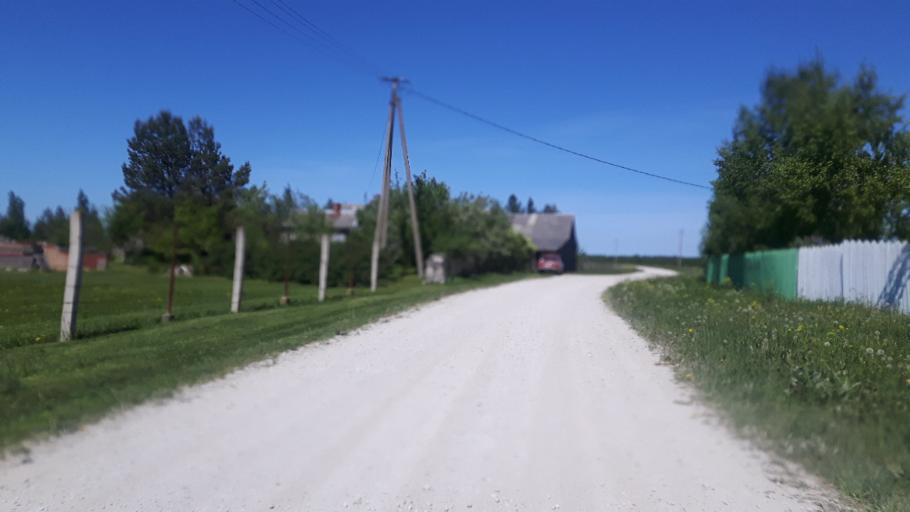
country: EE
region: Ida-Virumaa
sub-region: Toila vald
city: Voka
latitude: 59.3947
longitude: 27.6679
